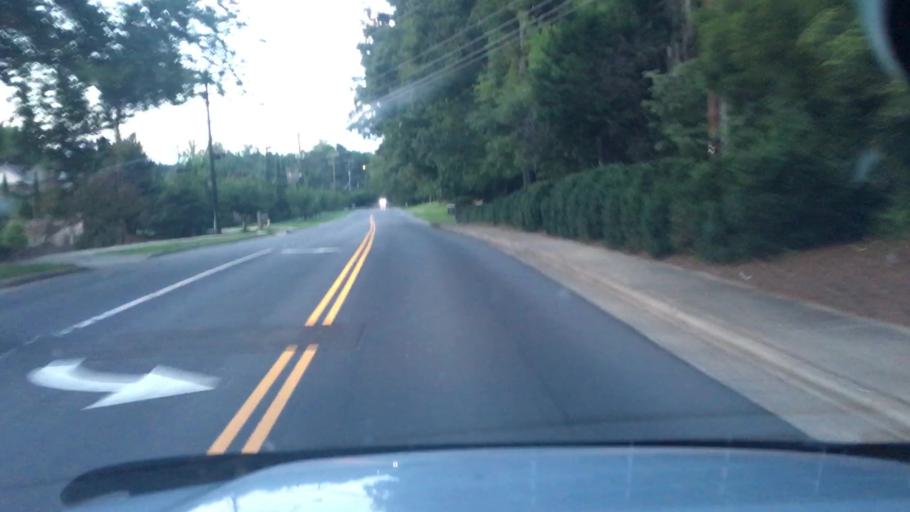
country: US
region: North Carolina
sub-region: Mecklenburg County
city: Pineville
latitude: 35.1232
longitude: -80.8175
